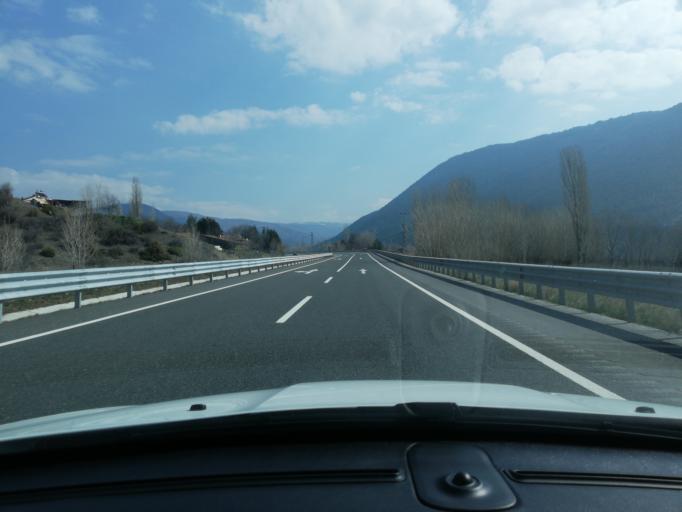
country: TR
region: Cankiri
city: Ilgaz
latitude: 40.9629
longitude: 33.6786
